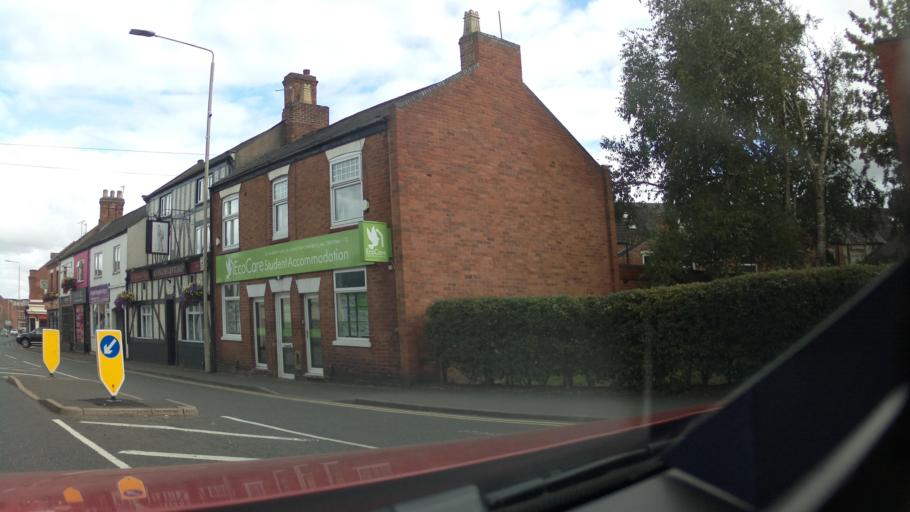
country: GB
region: England
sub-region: Leicestershire
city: Loughborough
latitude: 52.7725
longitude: -1.2145
